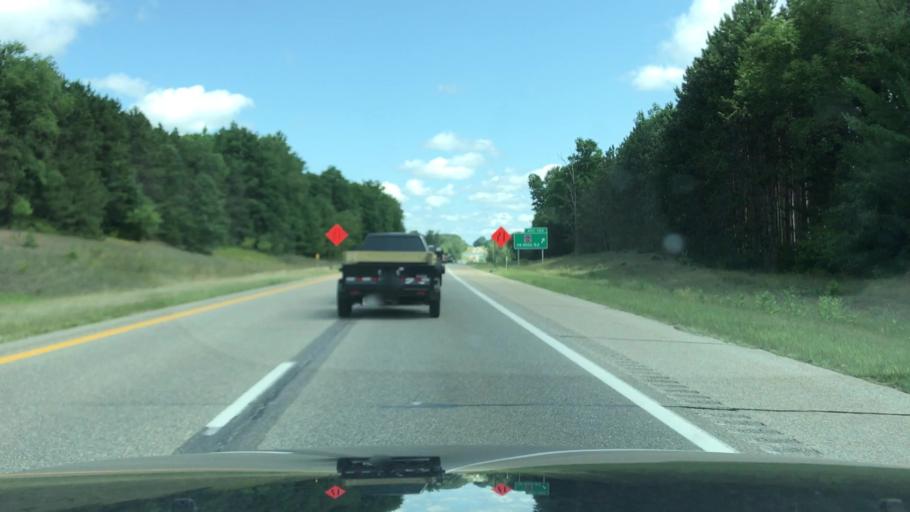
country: US
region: Michigan
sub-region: Mecosta County
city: Big Rapids
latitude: 43.7339
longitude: -85.5325
